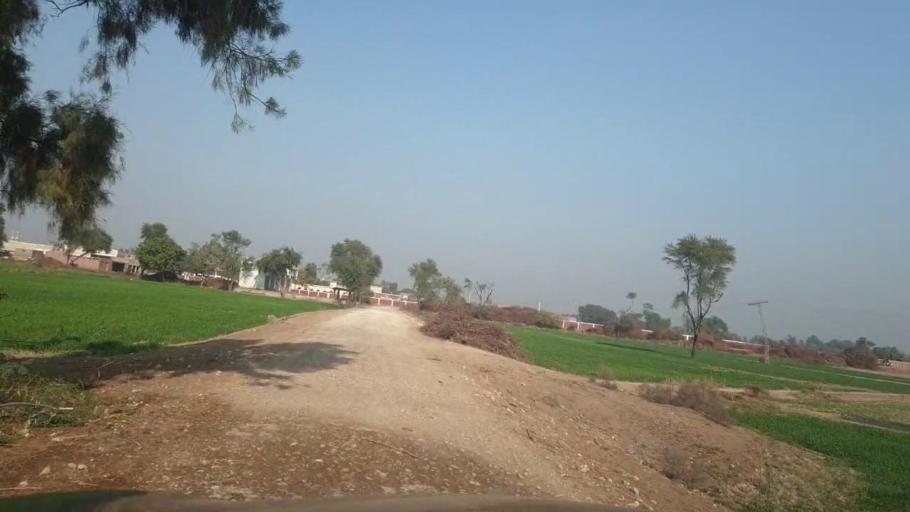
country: PK
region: Sindh
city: Ubauro
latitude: 28.1011
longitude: 69.8431
